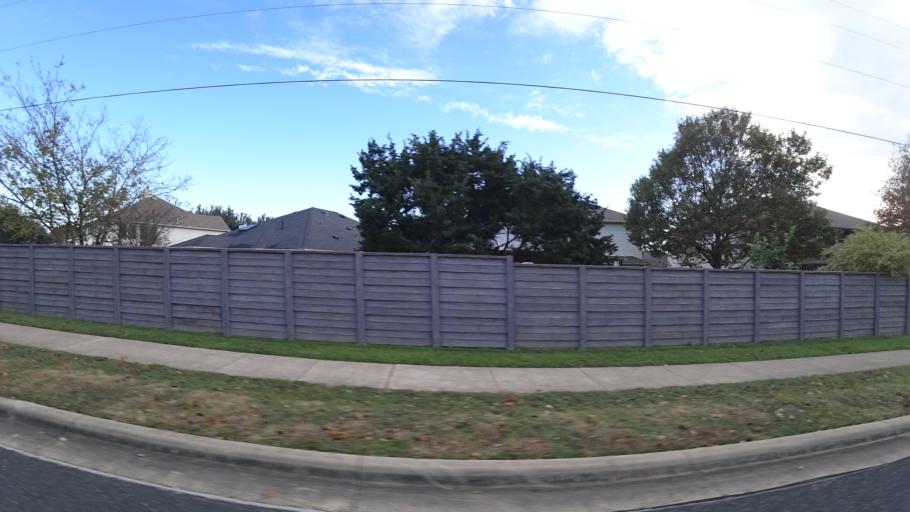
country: US
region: Texas
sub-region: Williamson County
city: Brushy Creek
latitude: 30.5007
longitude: -97.7338
